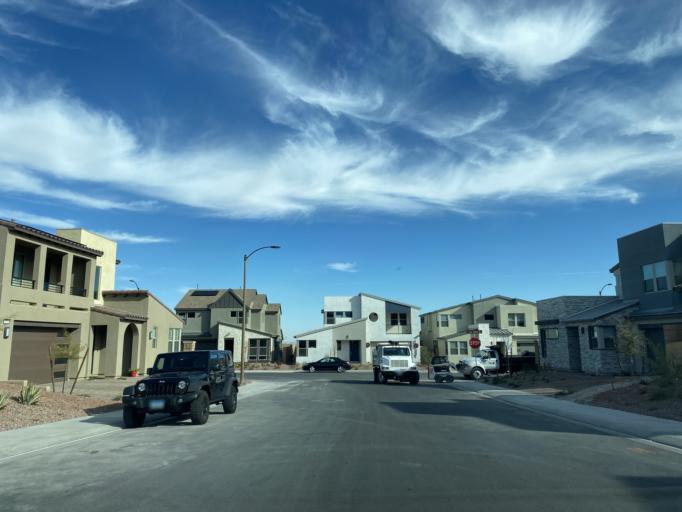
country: US
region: Nevada
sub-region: Clark County
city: Summerlin South
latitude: 36.3111
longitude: -115.3190
